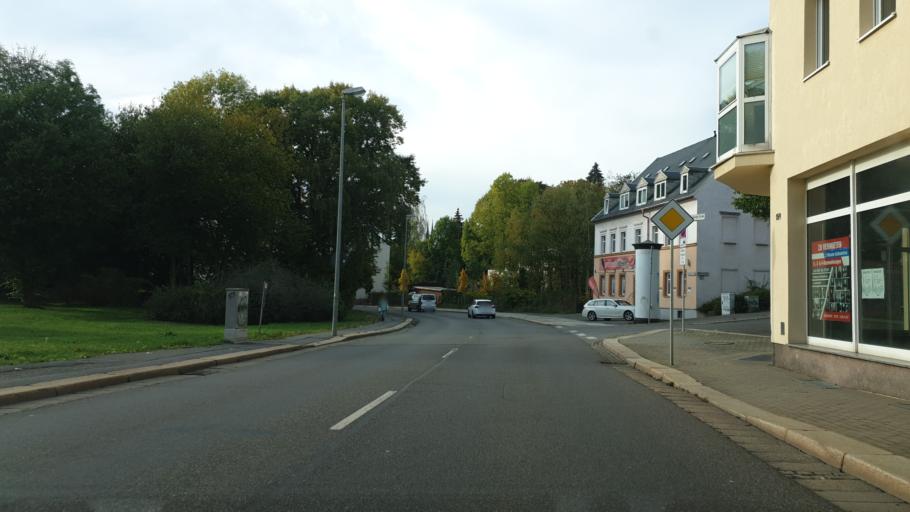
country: DE
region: Saxony
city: Chemnitz
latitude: 50.8320
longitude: 12.9481
